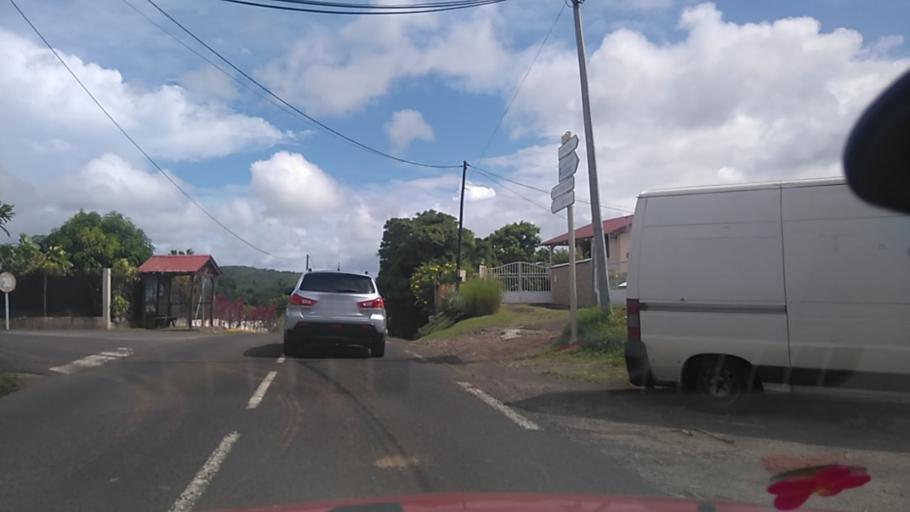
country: MQ
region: Martinique
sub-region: Martinique
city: Saint-Esprit
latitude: 14.5706
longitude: -60.9336
